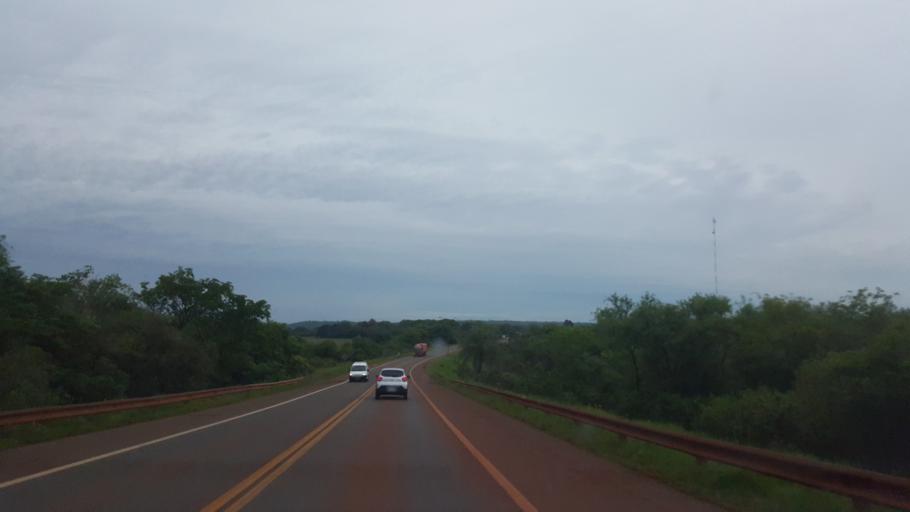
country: AR
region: Misiones
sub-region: Departamento de Apostoles
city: San Jose
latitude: -27.7516
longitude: -55.7855
